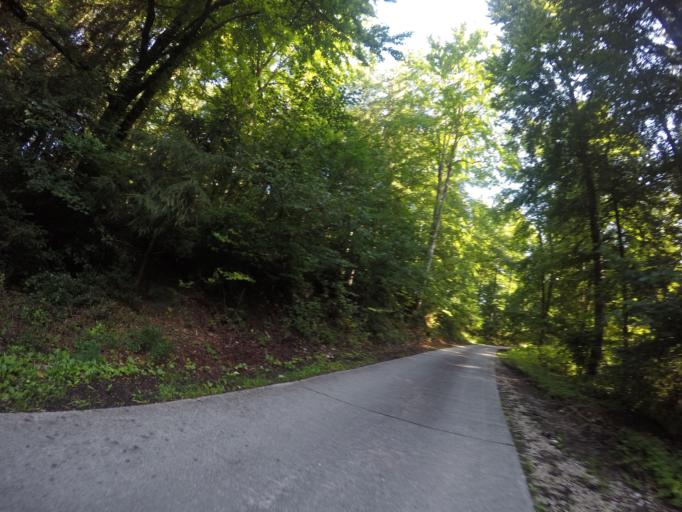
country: DE
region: Baden-Wuerttemberg
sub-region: Tuebingen Region
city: Schelklingen
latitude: 48.3918
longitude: 9.7366
